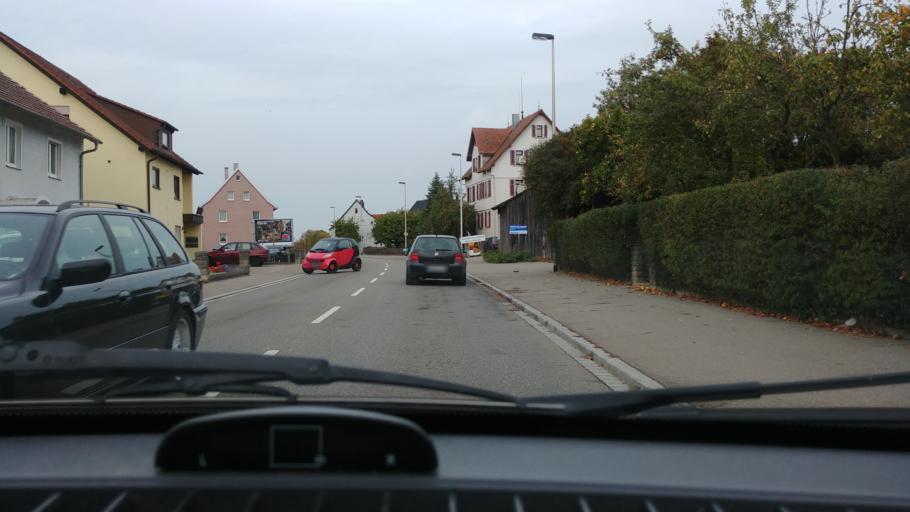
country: DE
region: Baden-Wuerttemberg
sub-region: Regierungsbezirk Stuttgart
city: Crailsheim
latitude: 49.1310
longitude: 10.0773
